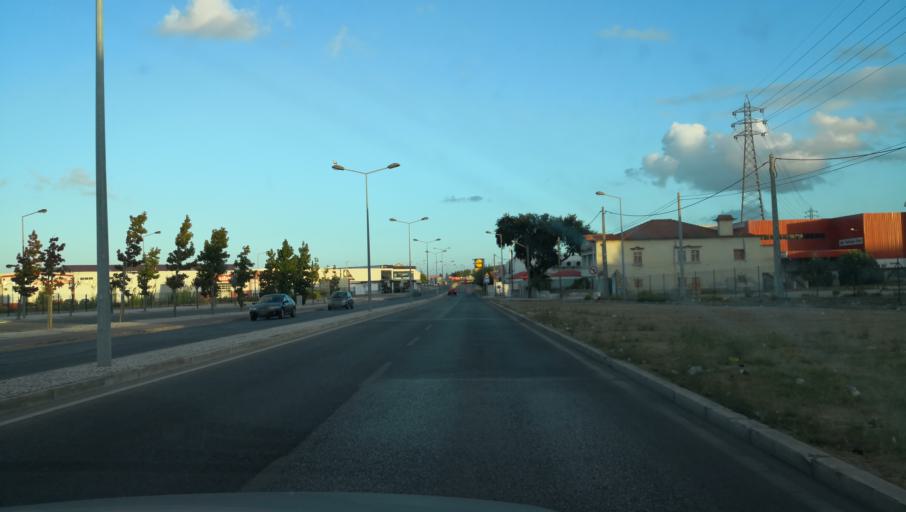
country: PT
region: Setubal
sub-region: Moita
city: Alhos Vedros
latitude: 38.6578
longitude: -9.0382
